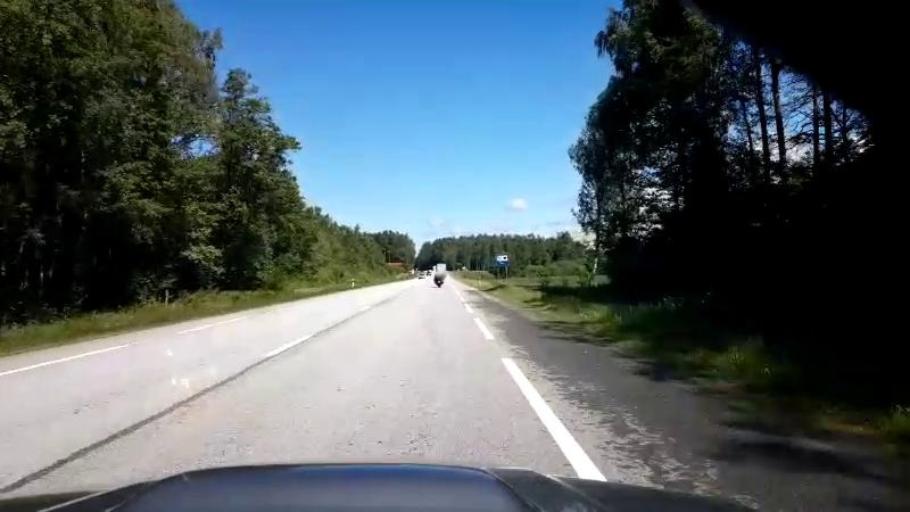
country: LV
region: Saulkrastu
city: Saulkrasti
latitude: 57.4344
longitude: 24.4299
